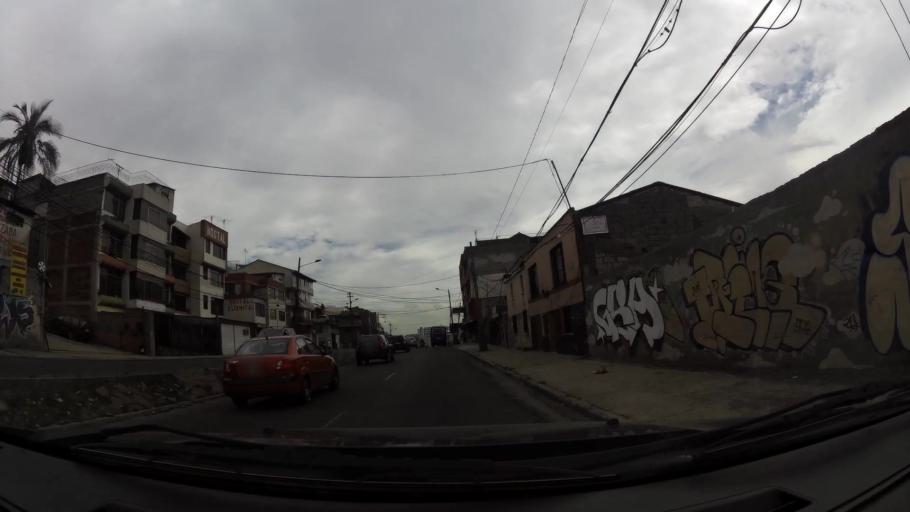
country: EC
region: Pichincha
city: Quito
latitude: -0.2175
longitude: -78.4911
